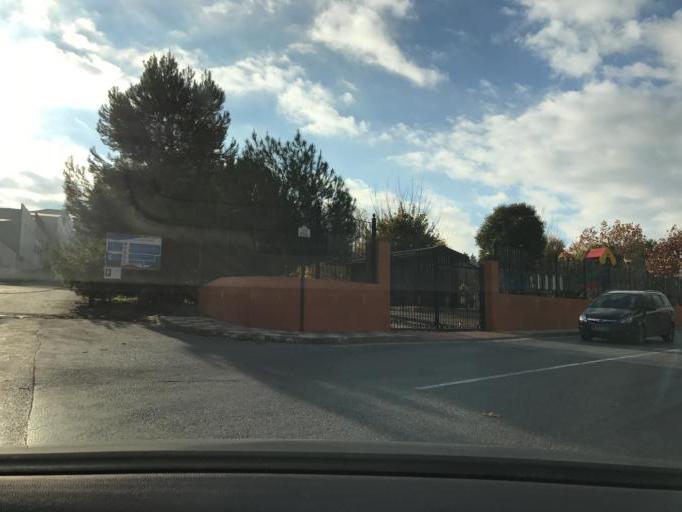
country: ES
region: Andalusia
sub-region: Provincia de Granada
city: Cajar
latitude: 37.1282
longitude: -3.5655
